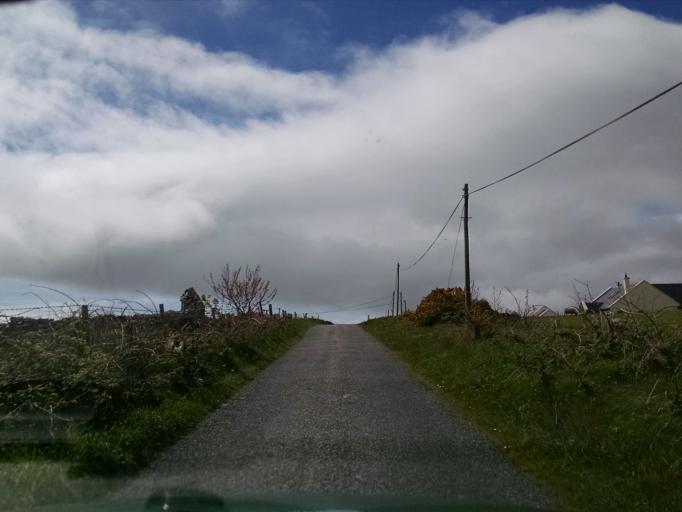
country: IE
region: Connaught
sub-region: County Galway
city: Clifden
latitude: 53.7393
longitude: -9.8559
